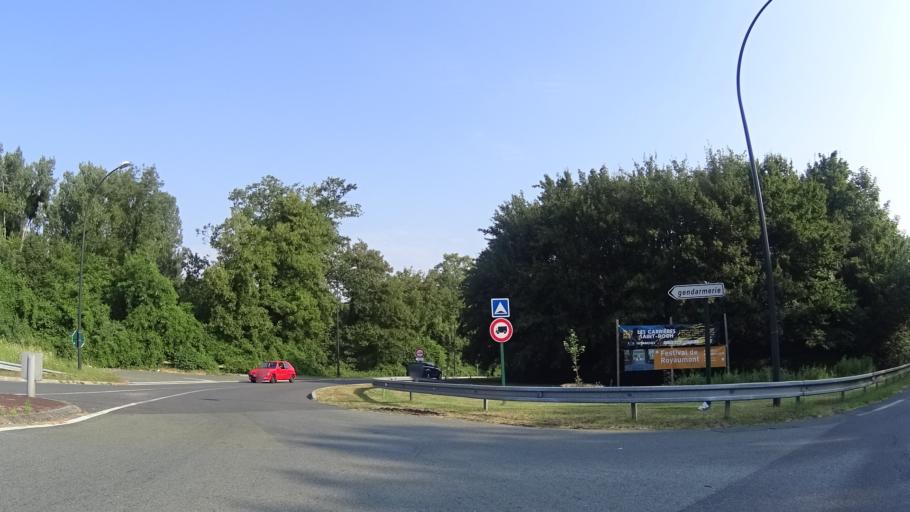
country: FR
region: Ile-de-France
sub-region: Departement du Val-d'Oise
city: Luzarches
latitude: 49.1022
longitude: 2.4227
